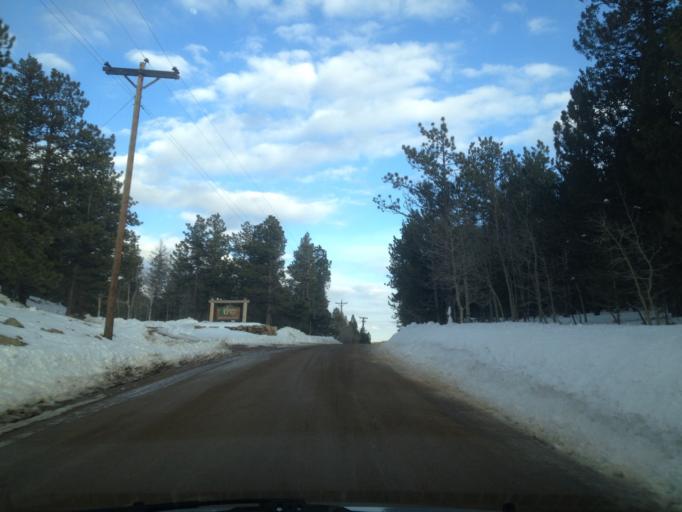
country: US
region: Colorado
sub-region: Boulder County
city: Nederland
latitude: 40.1247
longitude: -105.4607
